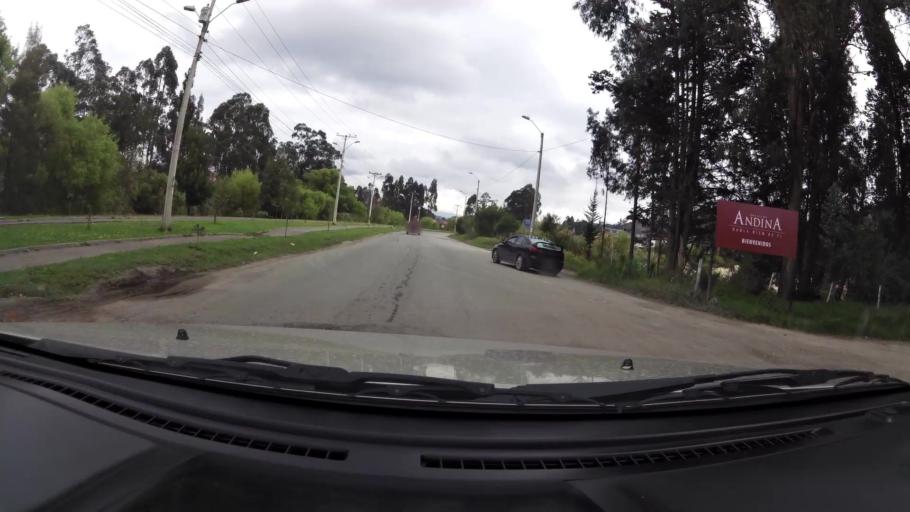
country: EC
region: Azuay
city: Cuenca
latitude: -2.8950
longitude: -78.9665
